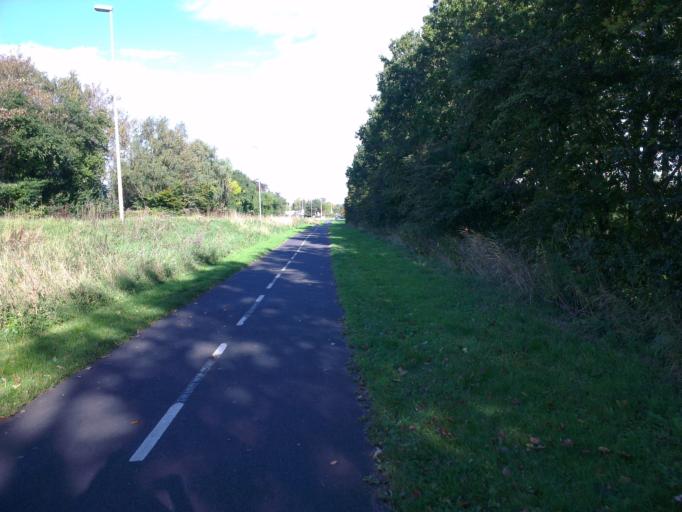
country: DK
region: Zealand
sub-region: Lejre Kommune
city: Ejby
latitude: 55.6855
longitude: 11.8487
